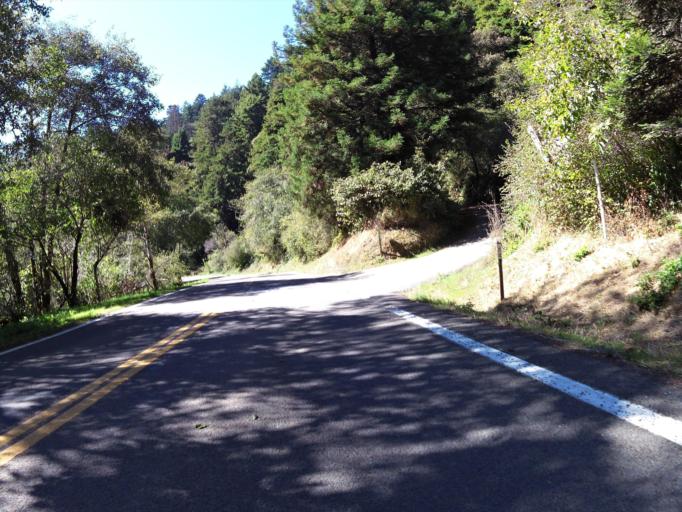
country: US
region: California
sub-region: Mendocino County
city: Fort Bragg
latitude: 39.7804
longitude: -123.8314
